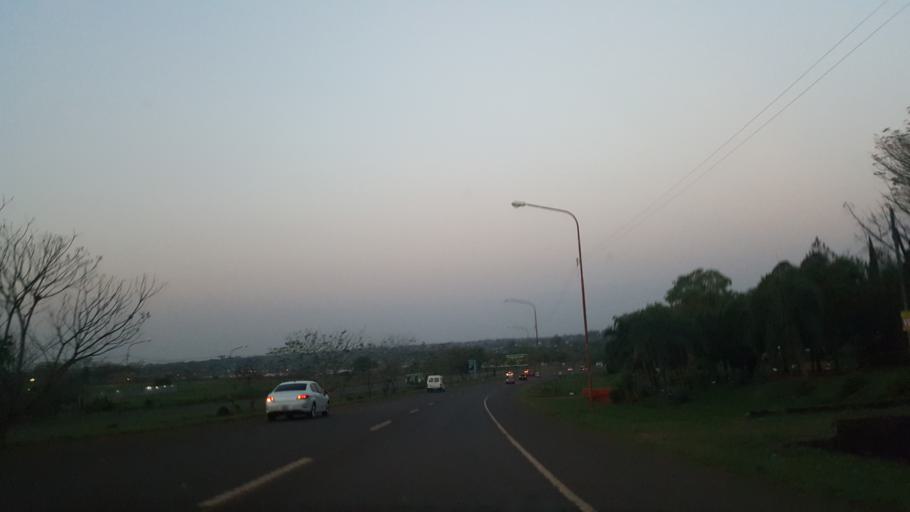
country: AR
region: Misiones
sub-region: Departamento de Capital
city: Posadas
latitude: -27.3992
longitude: -55.9626
